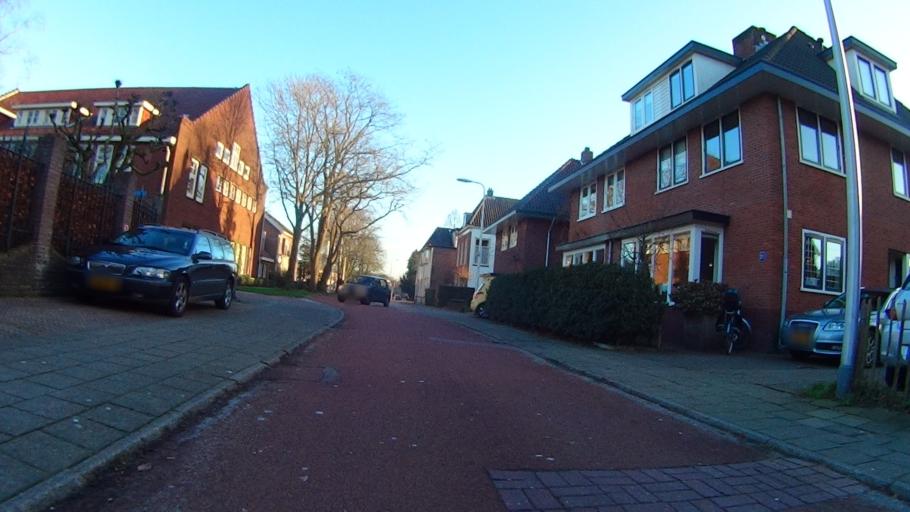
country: NL
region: Utrecht
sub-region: Gemeente Amersfoort
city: Randenbroek
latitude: 52.1543
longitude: 5.3968
